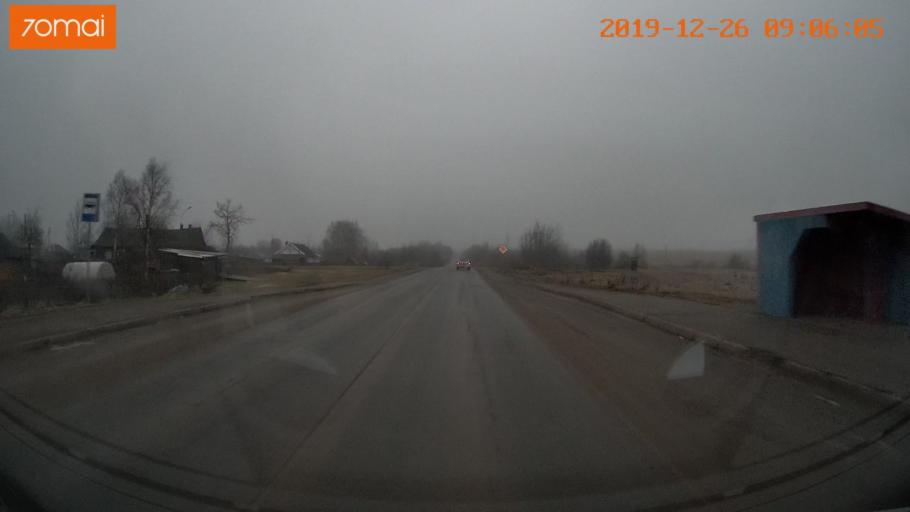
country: RU
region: Vologda
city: Gryazovets
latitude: 58.8324
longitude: 40.2549
